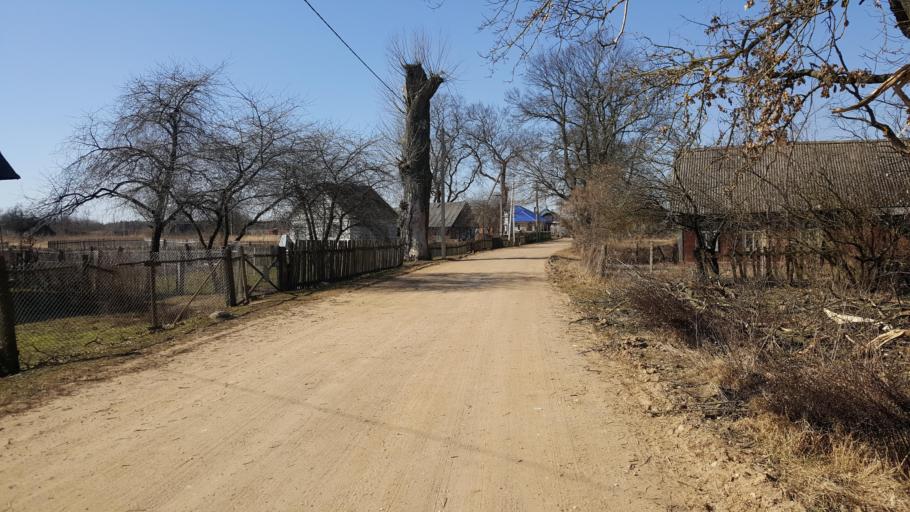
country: BY
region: Brest
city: Kamyanyets
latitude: 52.3728
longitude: 23.7831
